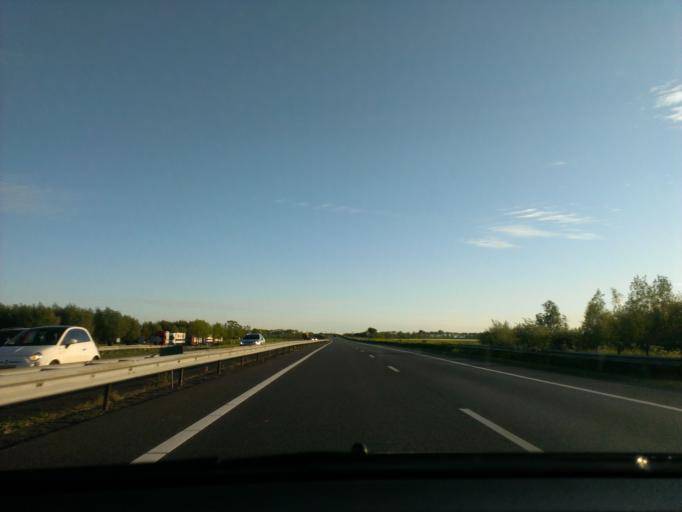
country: NL
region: South Holland
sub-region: Gemeente Oud-Beijerland
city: Oud-Beijerland
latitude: 51.7858
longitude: 4.4249
